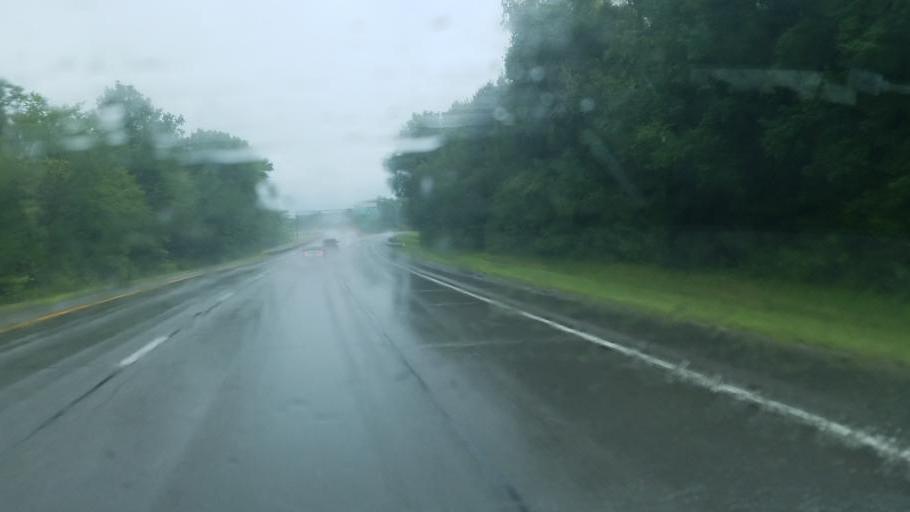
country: US
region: Ohio
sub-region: Trumbull County
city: Howland Center
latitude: 41.2412
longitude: -80.7629
